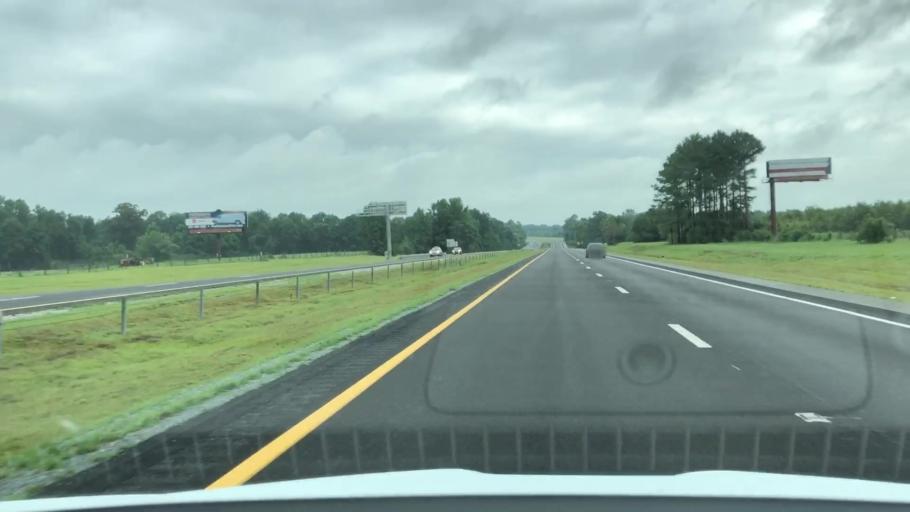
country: US
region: North Carolina
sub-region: Wayne County
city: Fremont
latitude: 35.5097
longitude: -77.9980
